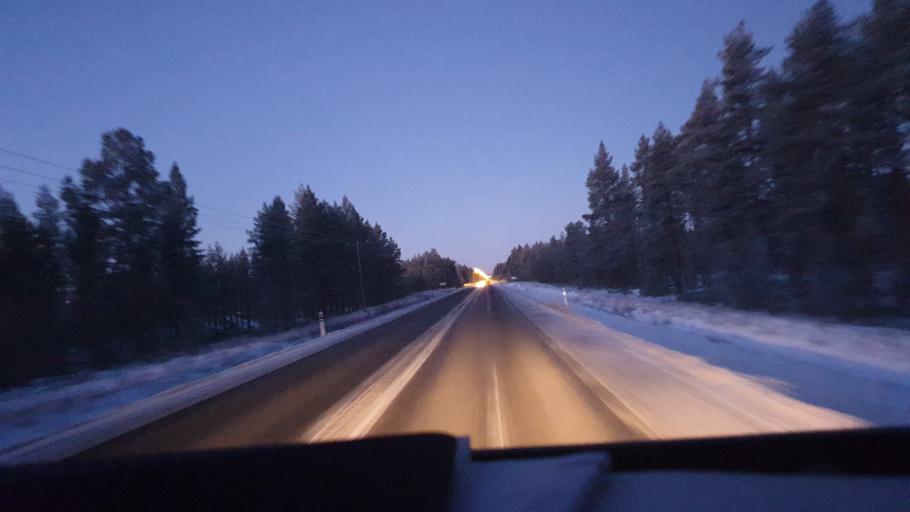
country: FI
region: Northern Ostrobothnia
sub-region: Raahe
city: Siikajoki
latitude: 64.6923
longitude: 24.6571
